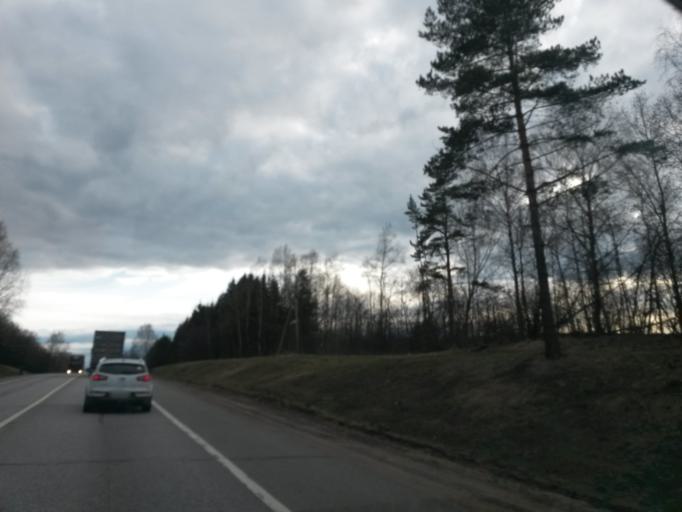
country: RU
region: Vladimir
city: Balakirevo
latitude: 56.6127
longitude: 38.6450
